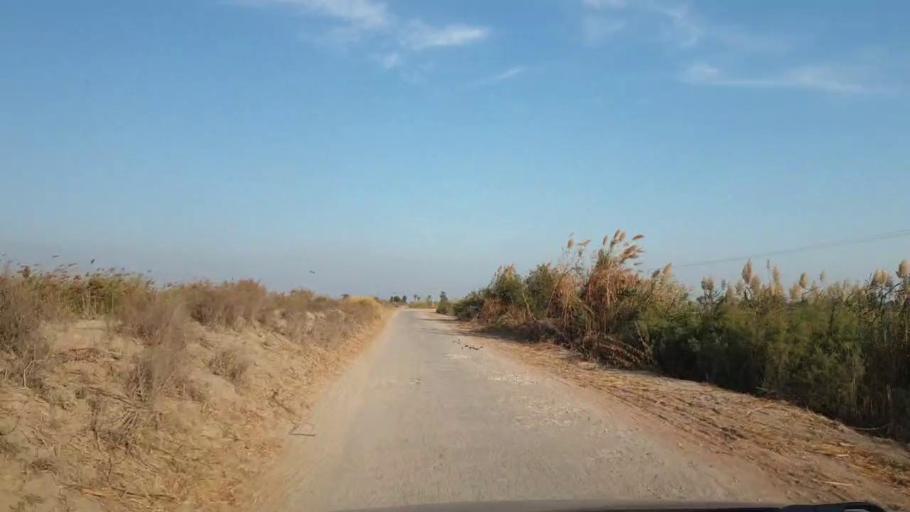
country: PK
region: Sindh
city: Khadro
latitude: 26.1781
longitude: 68.7513
